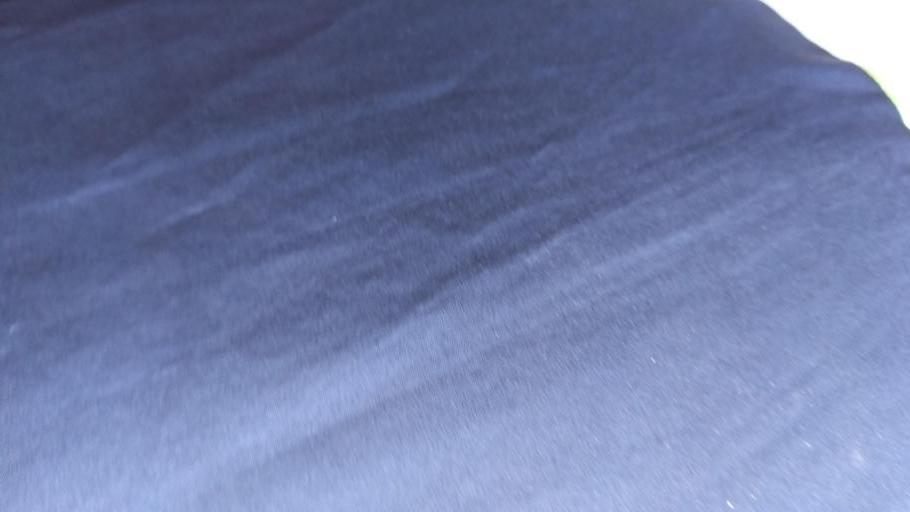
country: BD
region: Dhaka
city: Azimpur
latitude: 23.6644
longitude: 90.3306
